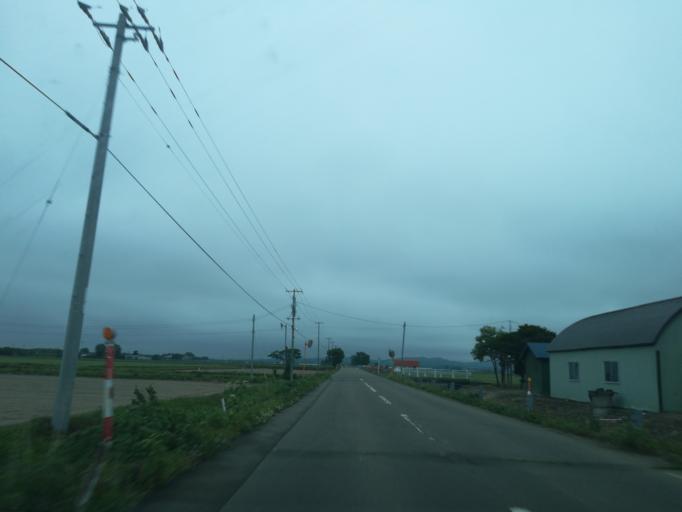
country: JP
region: Hokkaido
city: Iwamizawa
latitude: 43.1395
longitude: 141.7173
